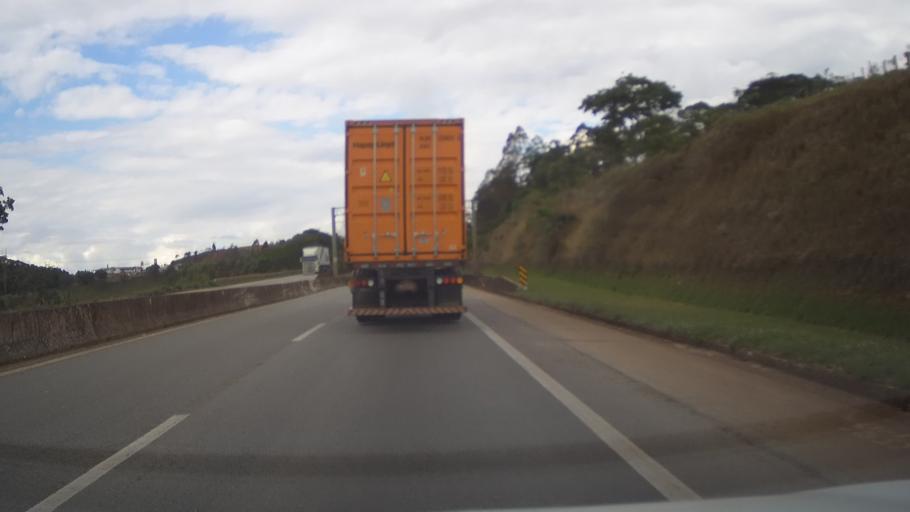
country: BR
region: Minas Gerais
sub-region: Igarape
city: Igarape
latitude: -20.2851
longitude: -44.4336
